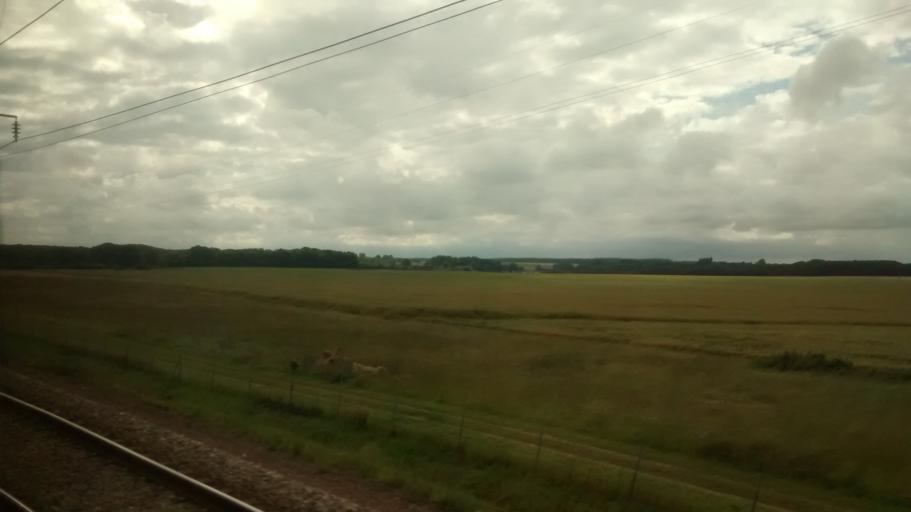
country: FR
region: Centre
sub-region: Departement d'Eure-et-Loir
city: Bonneval
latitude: 48.2025
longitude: 1.3931
